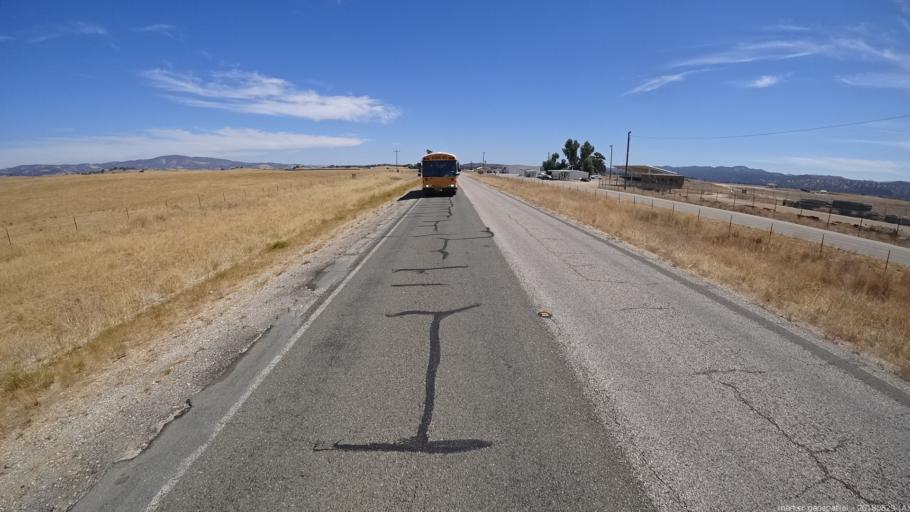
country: US
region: California
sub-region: Monterey County
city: King City
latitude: 35.9486
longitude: -121.1425
